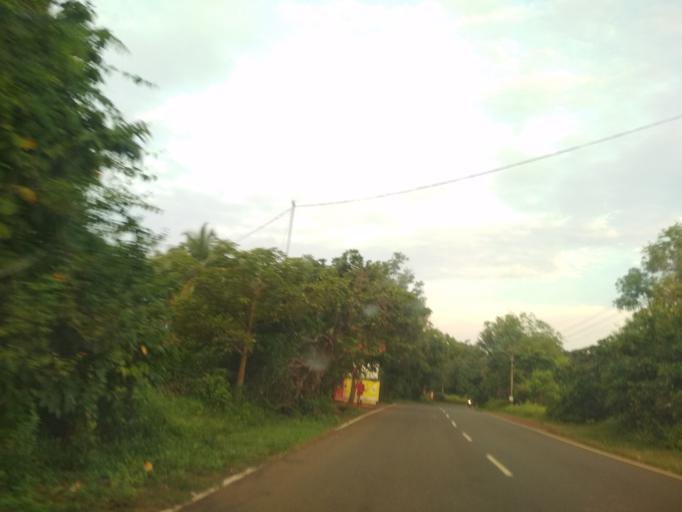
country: IN
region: Goa
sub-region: North Goa
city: Morjim
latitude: 15.6580
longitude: 73.7453
